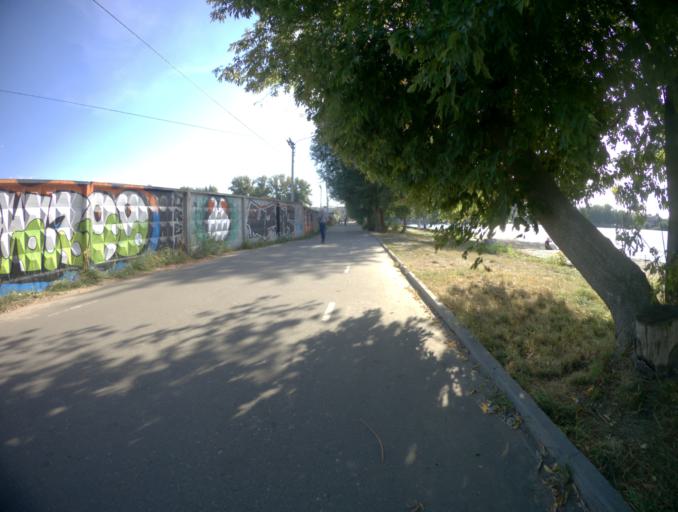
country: RU
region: Vladimir
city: Gus'-Khrustal'nyy
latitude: 55.6177
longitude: 40.6707
